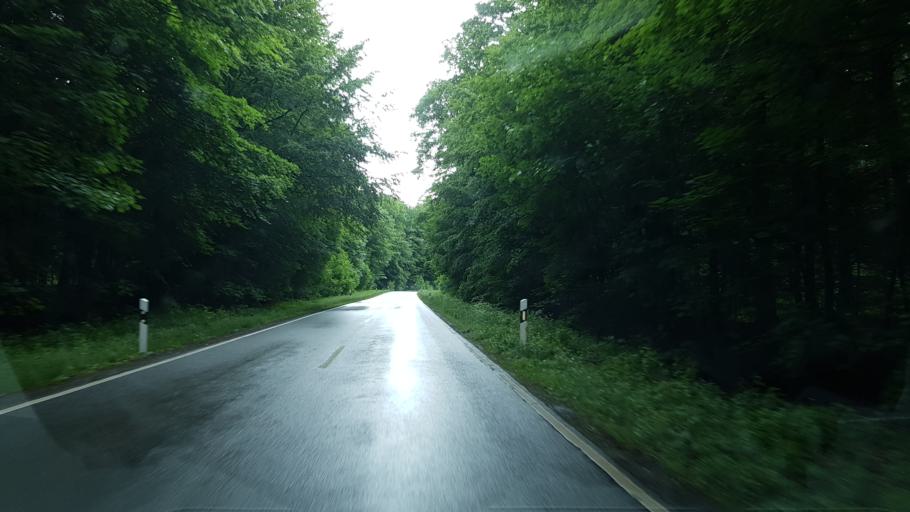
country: DE
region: Lower Saxony
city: Bodenfelde
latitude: 51.5880
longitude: 9.5152
